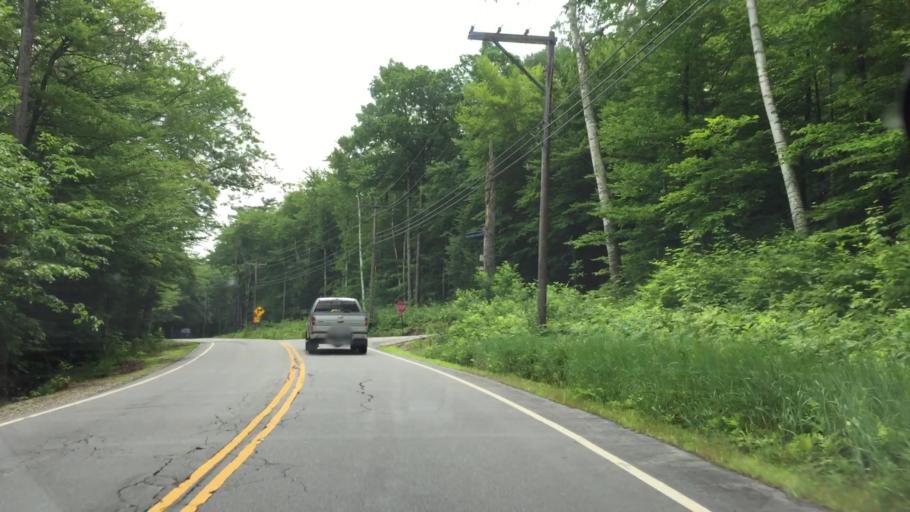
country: US
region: New Hampshire
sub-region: Grafton County
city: Holderness
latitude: 43.7567
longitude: -71.5568
